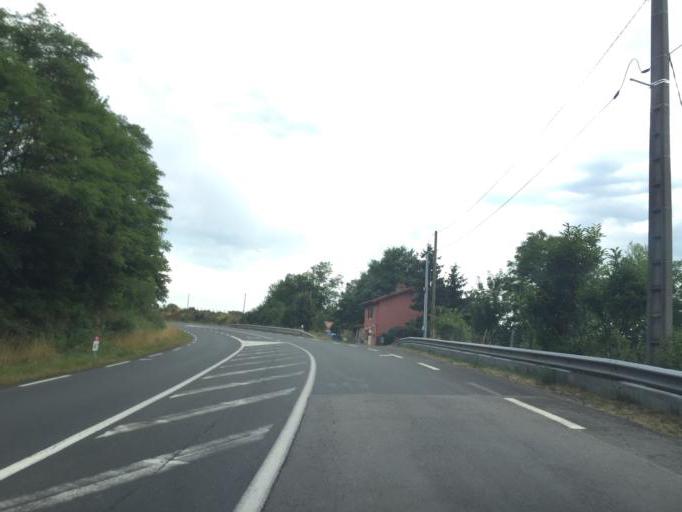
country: FR
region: Rhone-Alpes
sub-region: Departement de la Loire
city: Saint-Symphorien-de-Lay
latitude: 45.9535
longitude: 4.1921
